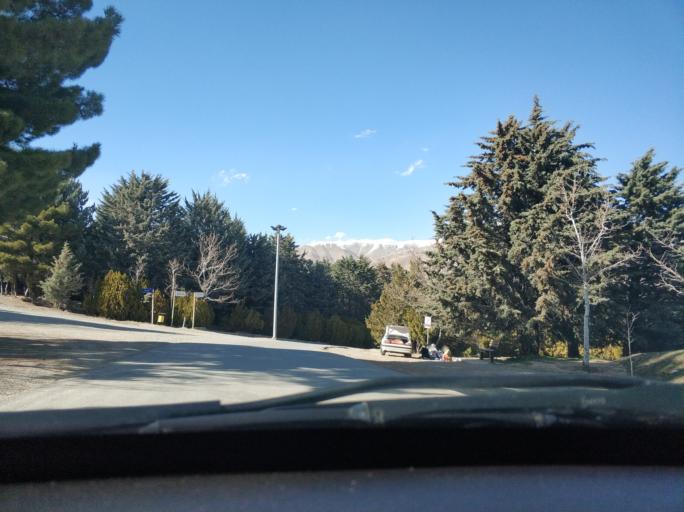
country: IR
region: Tehran
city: Tajrish
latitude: 35.8017
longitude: 51.5674
